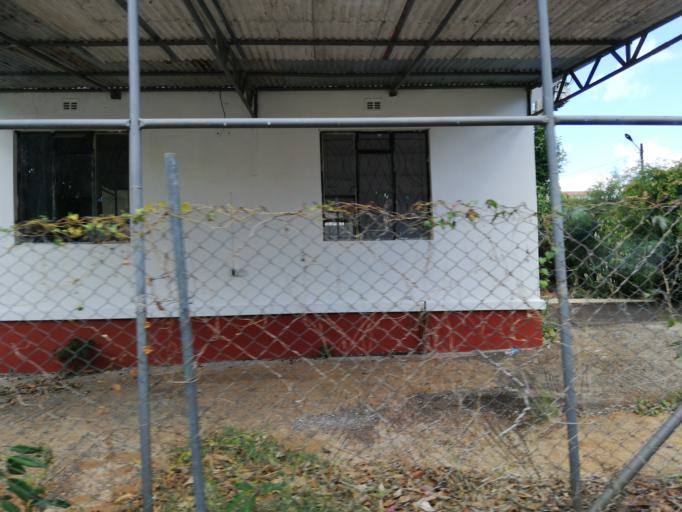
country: MU
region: Moka
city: Moka
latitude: -20.2122
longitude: 57.4739
